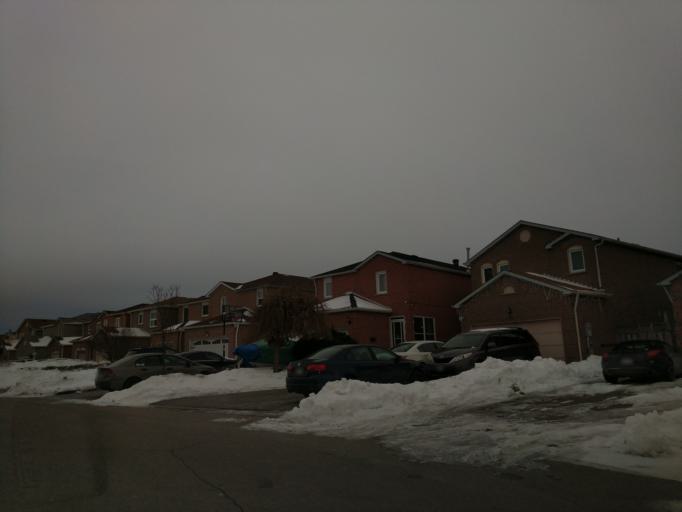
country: CA
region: Ontario
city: Markham
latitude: 43.8427
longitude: -79.2707
